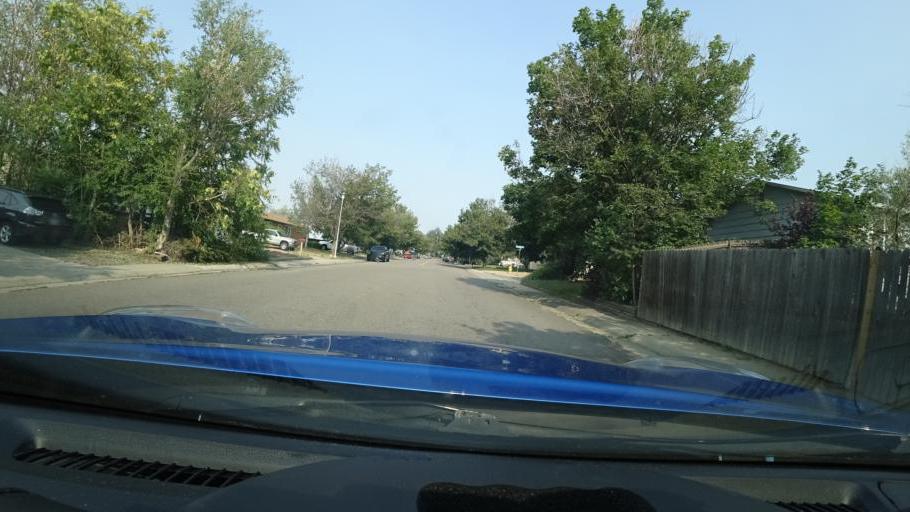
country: US
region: Colorado
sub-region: Adams County
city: Aurora
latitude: 39.6670
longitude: -104.8020
